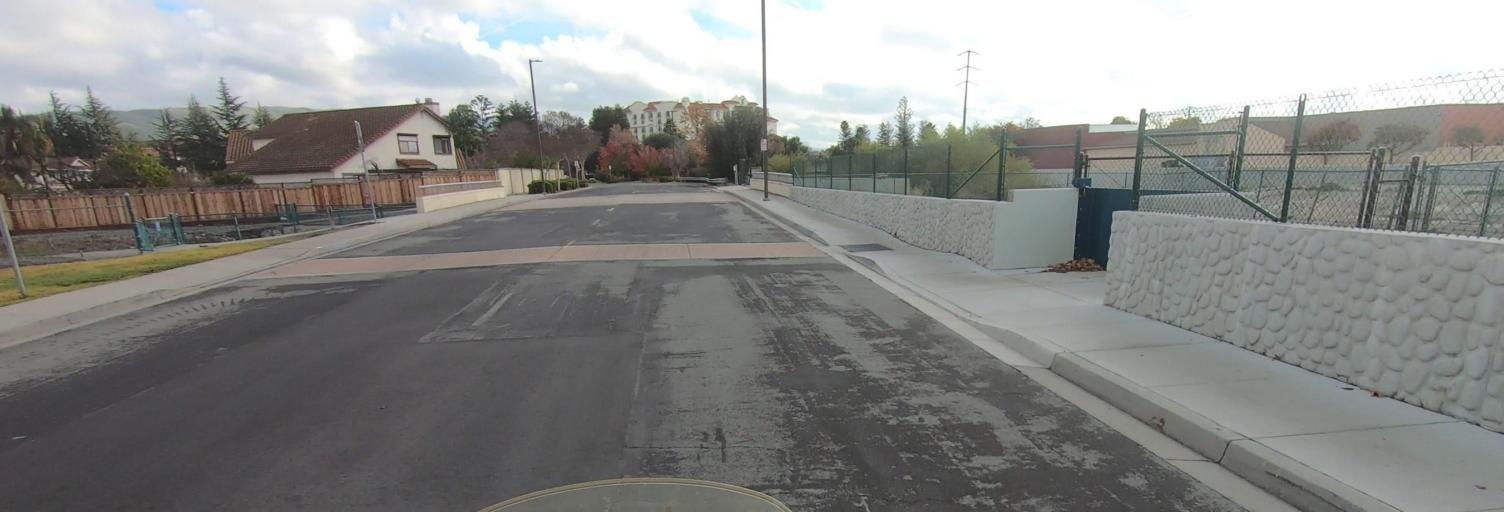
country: US
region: California
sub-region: Santa Clara County
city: Milpitas
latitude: 37.4365
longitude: -121.8952
